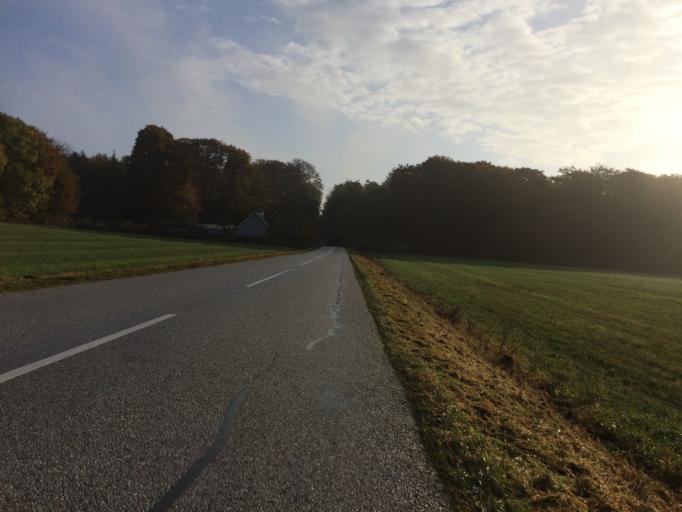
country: DK
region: Zealand
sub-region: Ringsted Kommune
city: Ringsted
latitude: 55.4894
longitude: 11.7892
